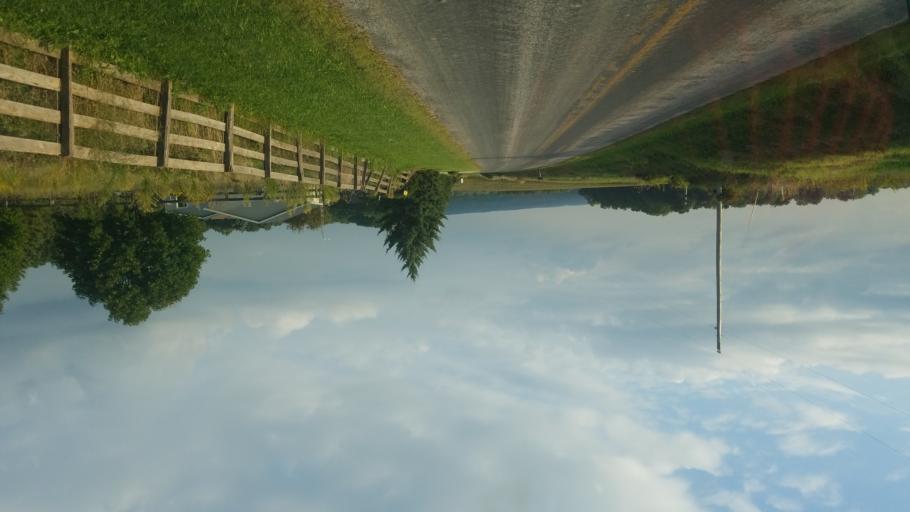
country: US
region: Ohio
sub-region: Wayne County
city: Shreve
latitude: 40.7369
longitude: -82.1303
